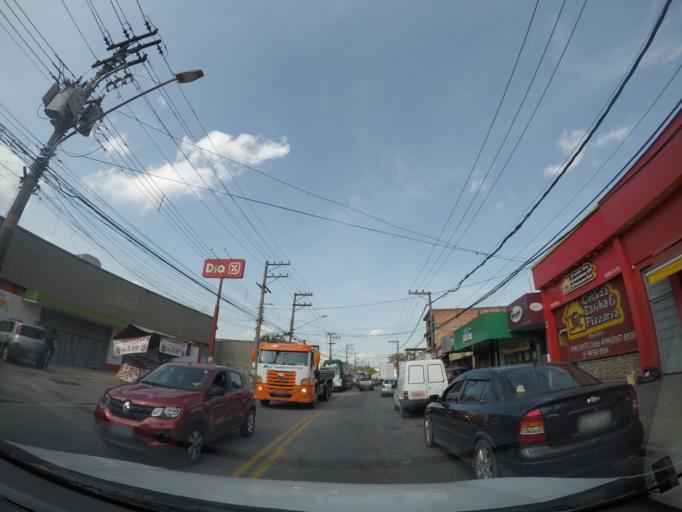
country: BR
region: Sao Paulo
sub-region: Guarulhos
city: Guarulhos
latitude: -23.4306
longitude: -46.4374
